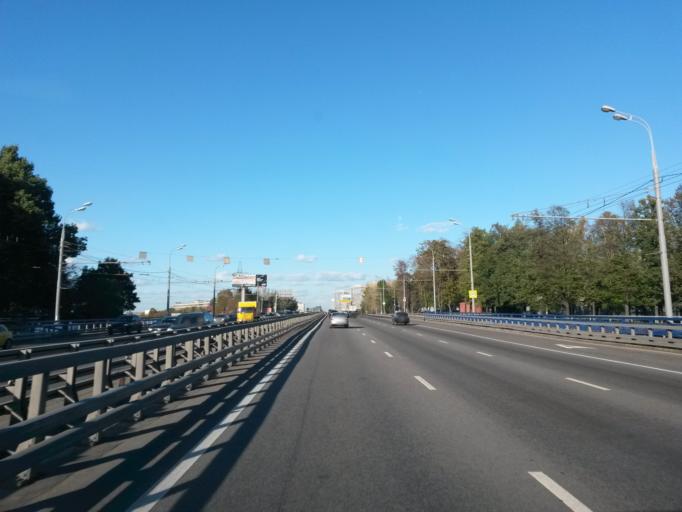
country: RU
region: Moscow
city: Nagornyy
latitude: 55.6659
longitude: 37.6221
